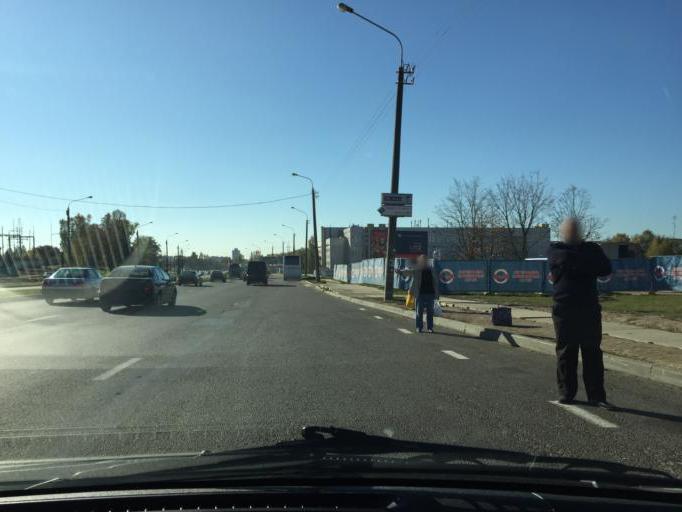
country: BY
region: Minsk
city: Syenitsa
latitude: 53.8428
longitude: 27.5338
